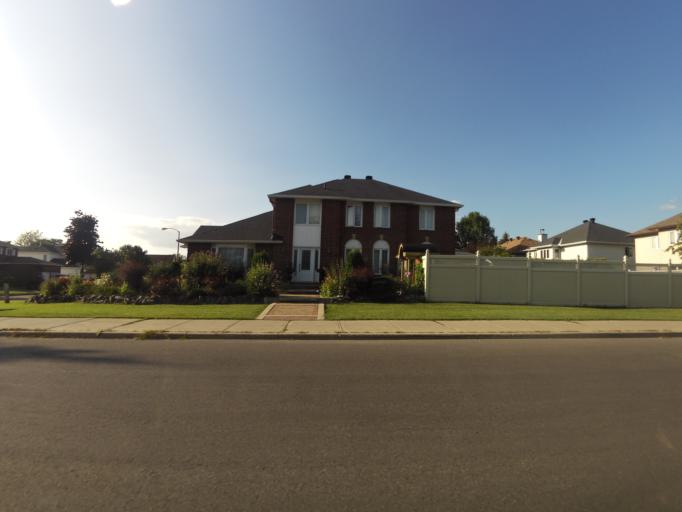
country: CA
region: Ontario
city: Clarence-Rockland
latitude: 45.4852
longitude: -75.4818
